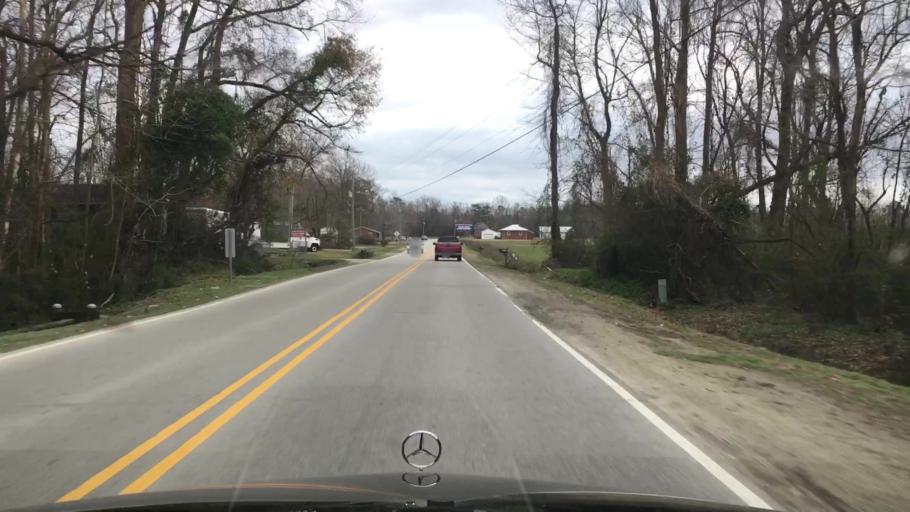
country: US
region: North Carolina
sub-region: Onslow County
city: Richlands
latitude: 34.8796
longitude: -77.5201
